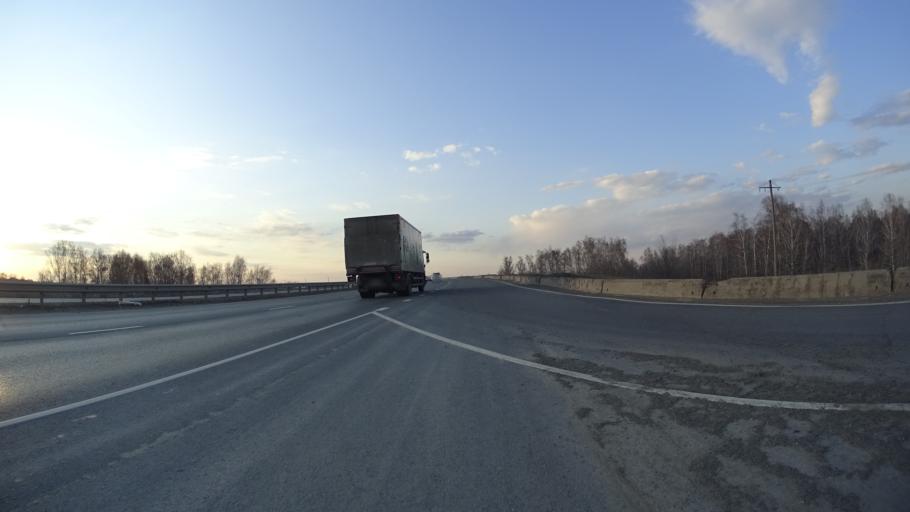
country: RU
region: Chelyabinsk
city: Novosineglazovskiy
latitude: 55.0377
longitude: 61.4416
